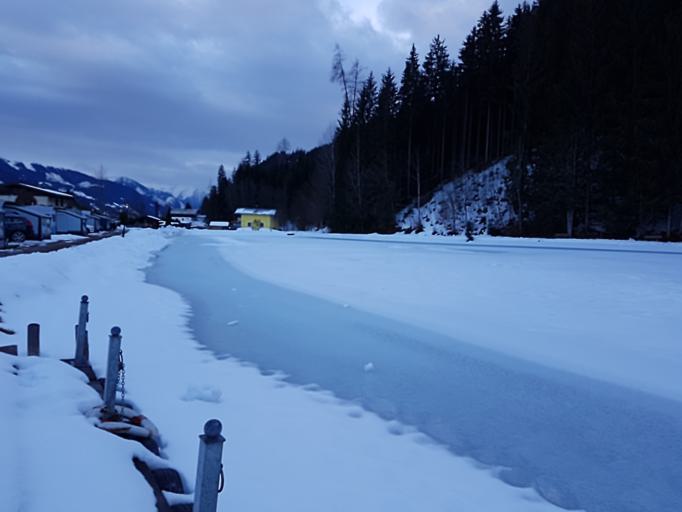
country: AT
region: Salzburg
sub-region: Politischer Bezirk Zell am See
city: Maishofen
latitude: 47.3773
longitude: 12.7951
